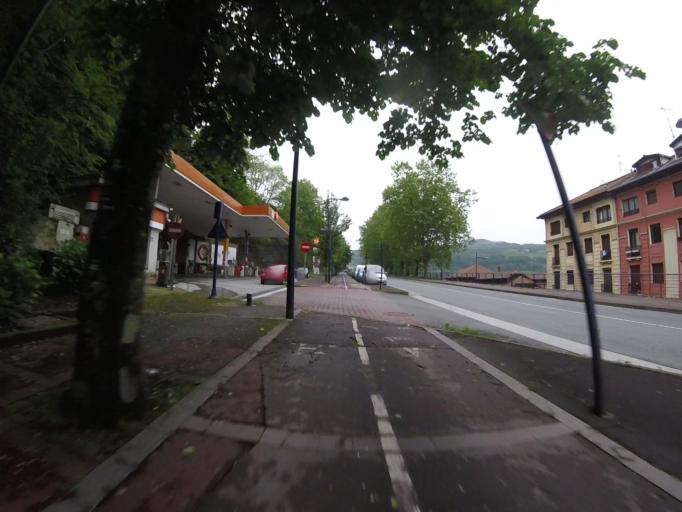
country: ES
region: Basque Country
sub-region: Provincia de Guipuzcoa
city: Errenteria
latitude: 43.3159
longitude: -1.9051
